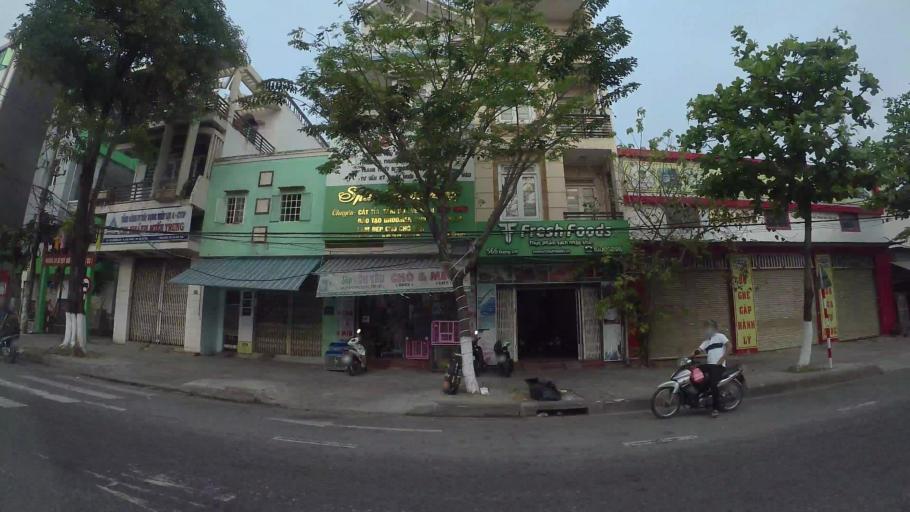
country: VN
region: Da Nang
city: Cam Le
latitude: 16.0313
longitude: 108.2239
